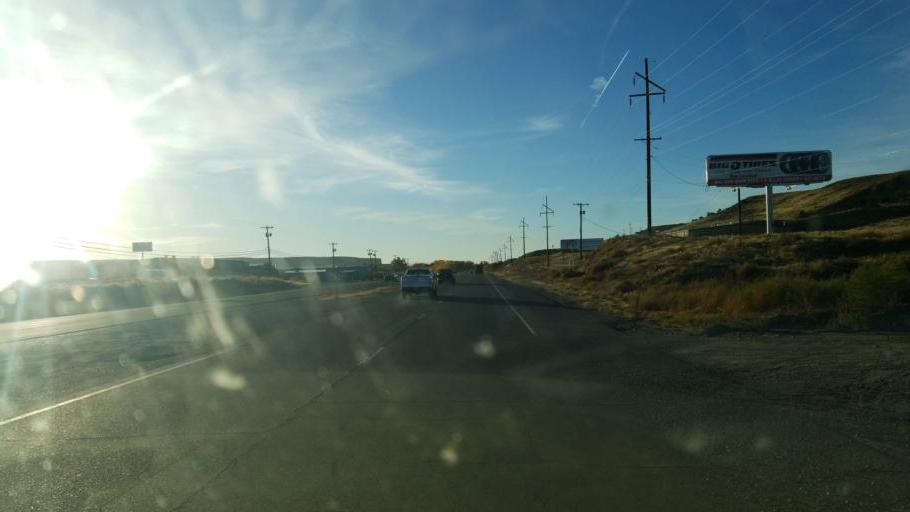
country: US
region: New Mexico
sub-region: San Juan County
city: Lee Acres
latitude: 36.7056
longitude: -108.1136
